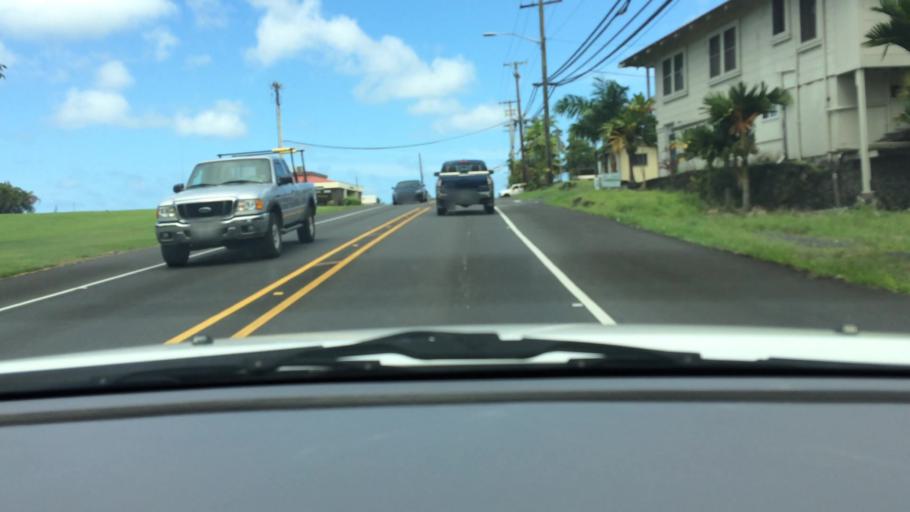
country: US
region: Hawaii
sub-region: Hawaii County
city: Hilo
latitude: 19.7117
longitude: -155.0741
